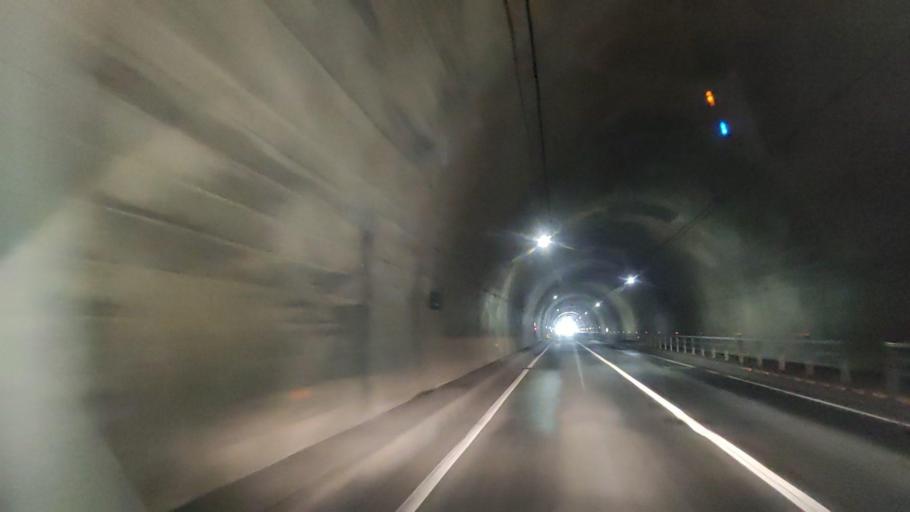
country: JP
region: Hokkaido
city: Sapporo
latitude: 43.0101
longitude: 141.1435
